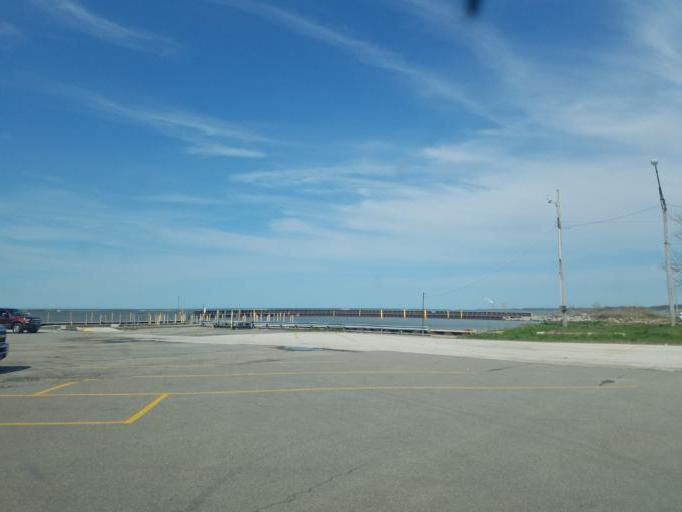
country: US
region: Ohio
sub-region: Lake County
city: Fairport Harbor
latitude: 41.7589
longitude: -81.2787
